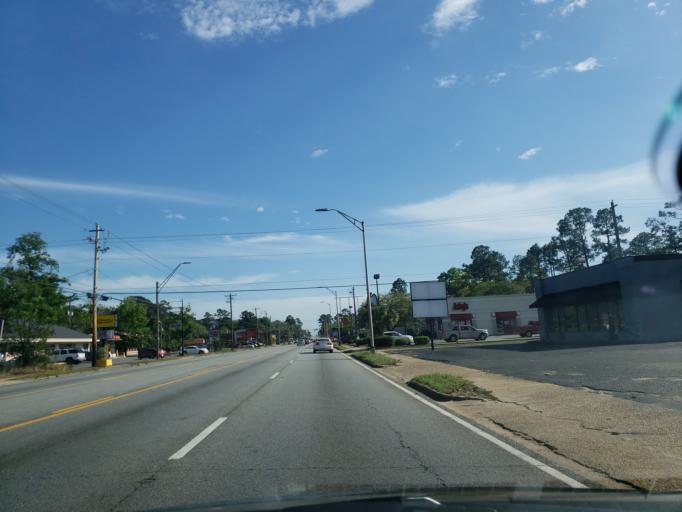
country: US
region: Georgia
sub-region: Dougherty County
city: Albany
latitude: 31.5928
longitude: -84.1761
